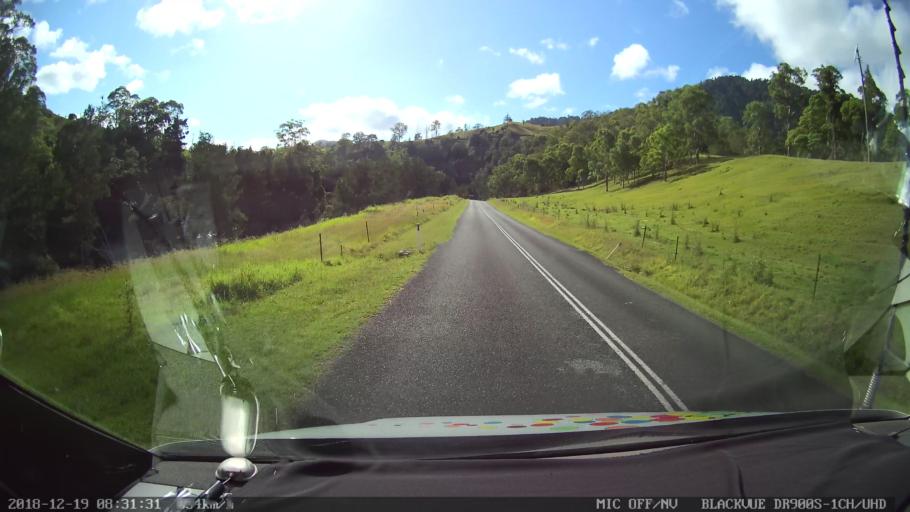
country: AU
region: New South Wales
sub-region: Kyogle
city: Kyogle
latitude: -28.3206
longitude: 152.9379
